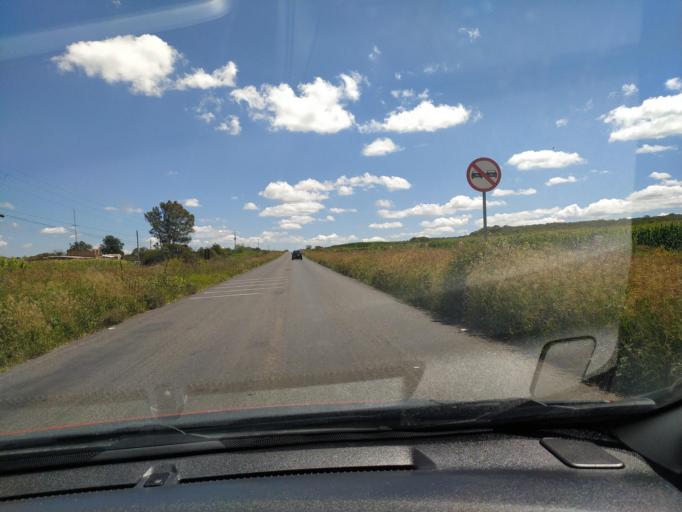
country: MX
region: Jalisco
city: San Julian
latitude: 21.0068
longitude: -102.1399
